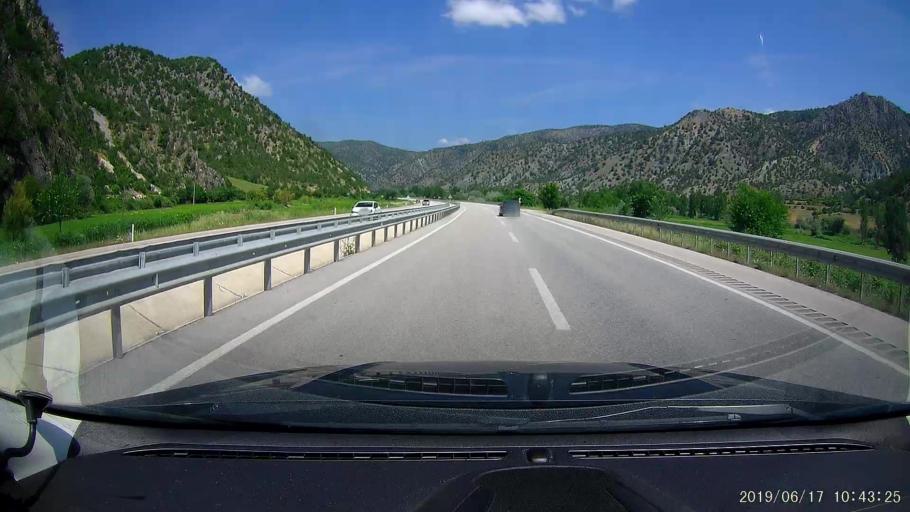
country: TR
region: Corum
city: Kargi
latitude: 41.0642
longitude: 34.5362
